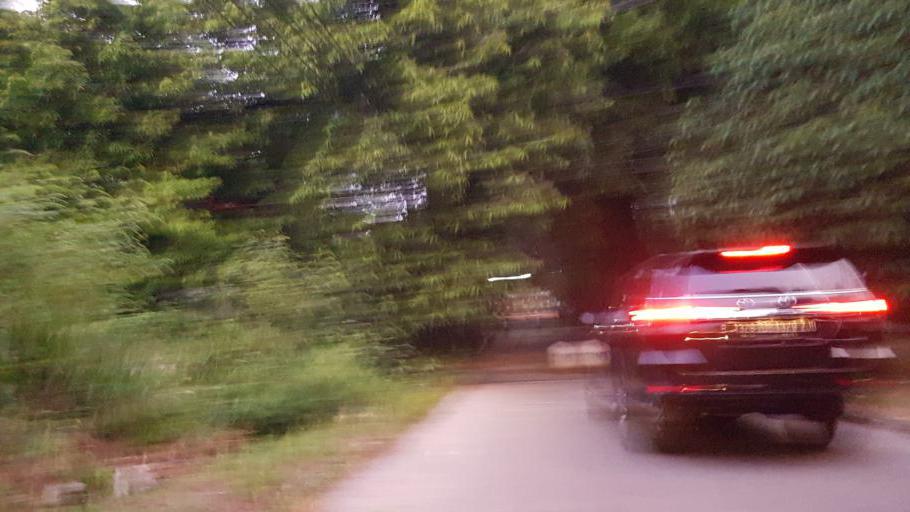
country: ID
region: West Java
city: Pamulang
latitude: -6.3431
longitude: 106.7812
